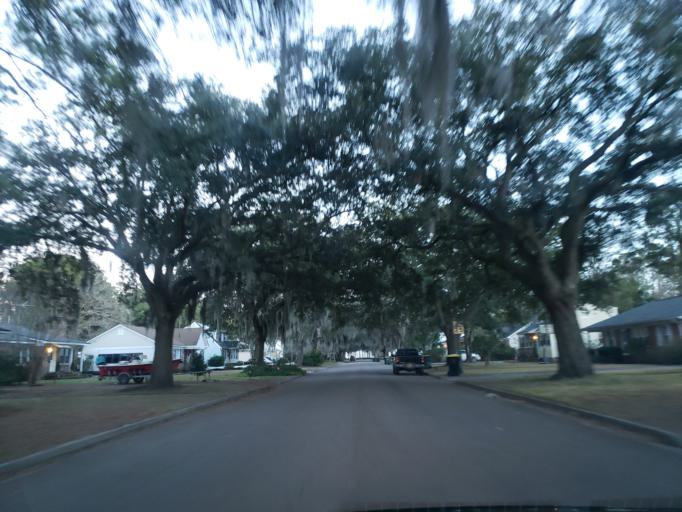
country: US
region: Georgia
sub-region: Chatham County
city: Thunderbolt
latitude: 32.0171
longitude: -81.0795
